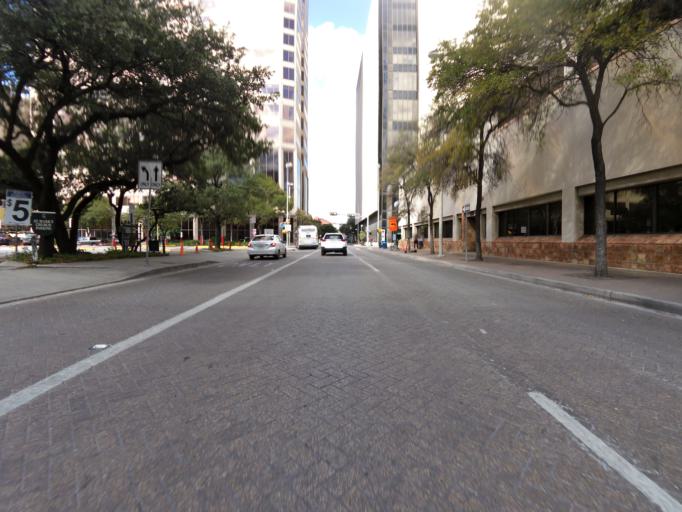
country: US
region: Texas
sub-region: Bexar County
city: San Antonio
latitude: 29.4287
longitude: -98.4898
